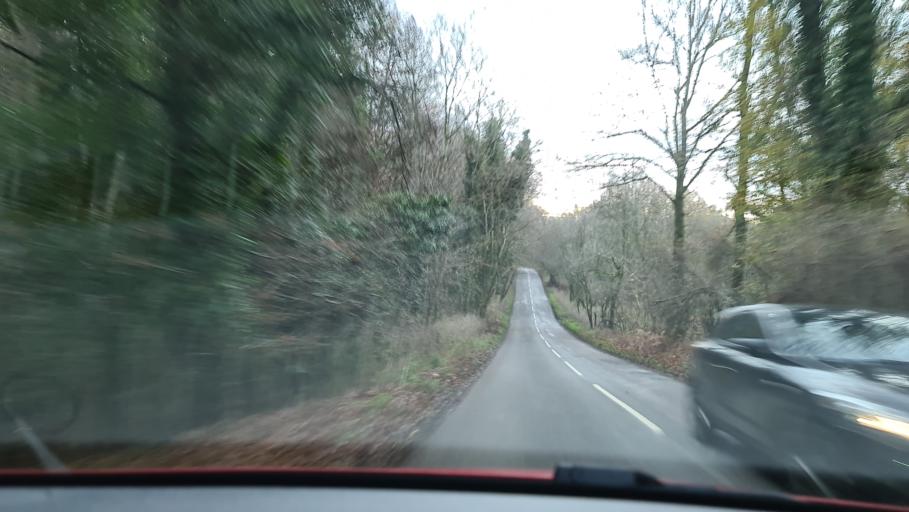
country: GB
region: England
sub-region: Buckinghamshire
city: Princes Risborough
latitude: 51.7069
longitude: -0.7816
